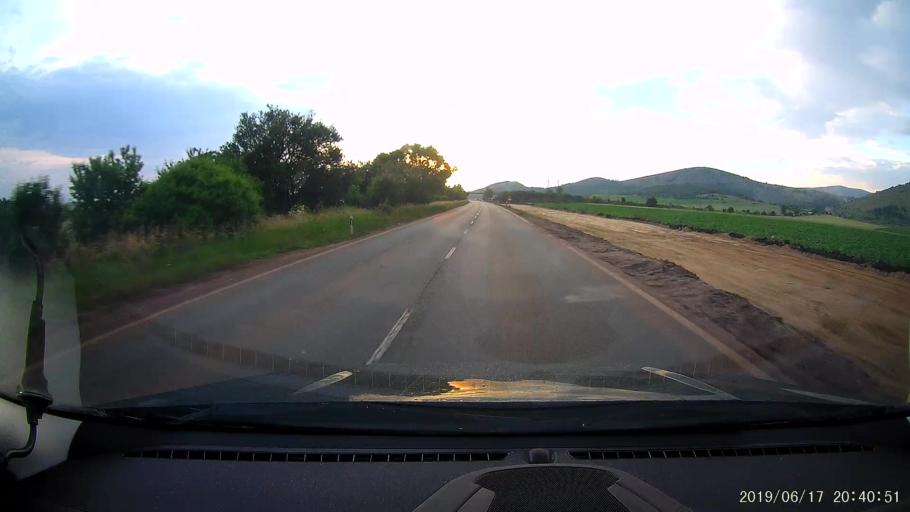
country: BG
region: Sofiya
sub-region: Obshtina Dragoman
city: Dragoman
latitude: 42.8907
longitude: 22.9790
